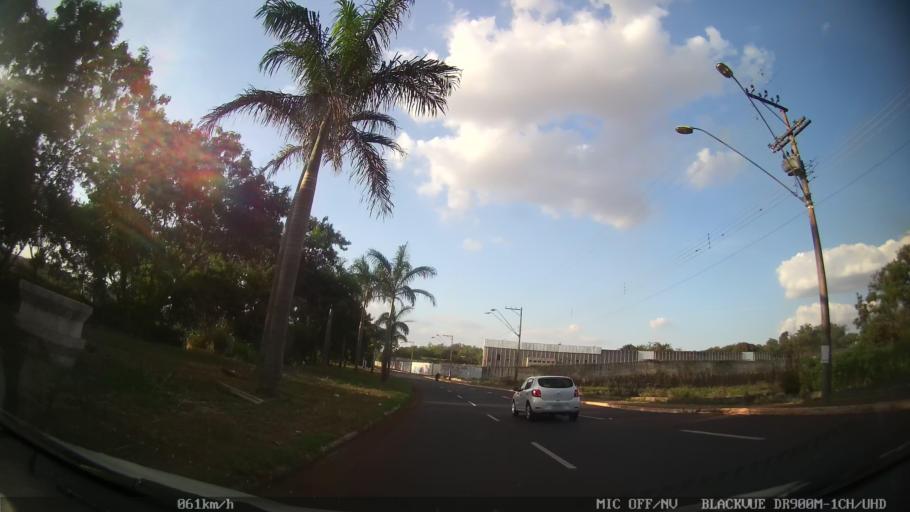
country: BR
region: Sao Paulo
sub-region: Ribeirao Preto
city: Ribeirao Preto
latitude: -21.1587
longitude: -47.8111
